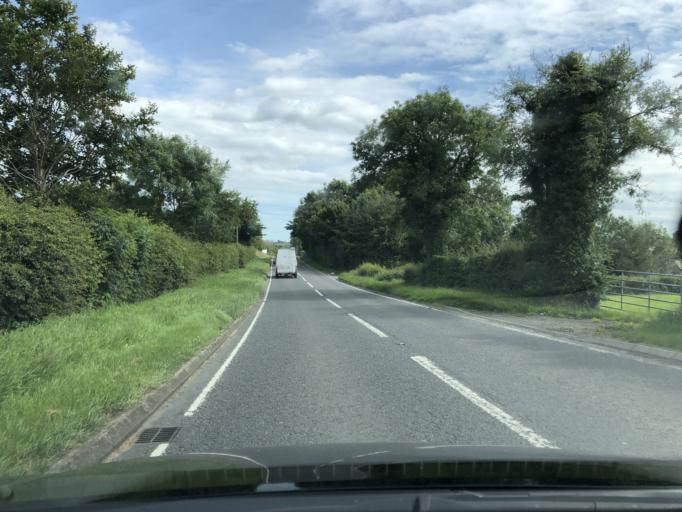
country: GB
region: Northern Ireland
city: Ballynahinch
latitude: 54.4236
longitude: -5.9206
